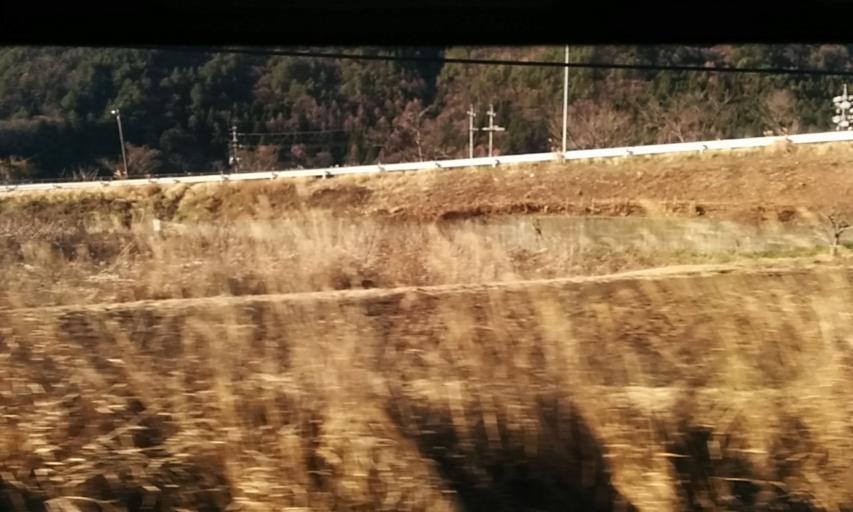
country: JP
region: Nagano
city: Ina
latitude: 35.8607
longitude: 137.7226
